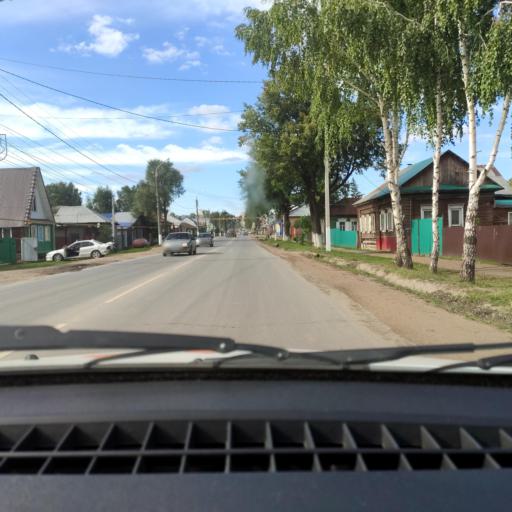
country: RU
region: Bashkortostan
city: Blagoveshchensk
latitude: 55.0349
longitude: 55.9651
